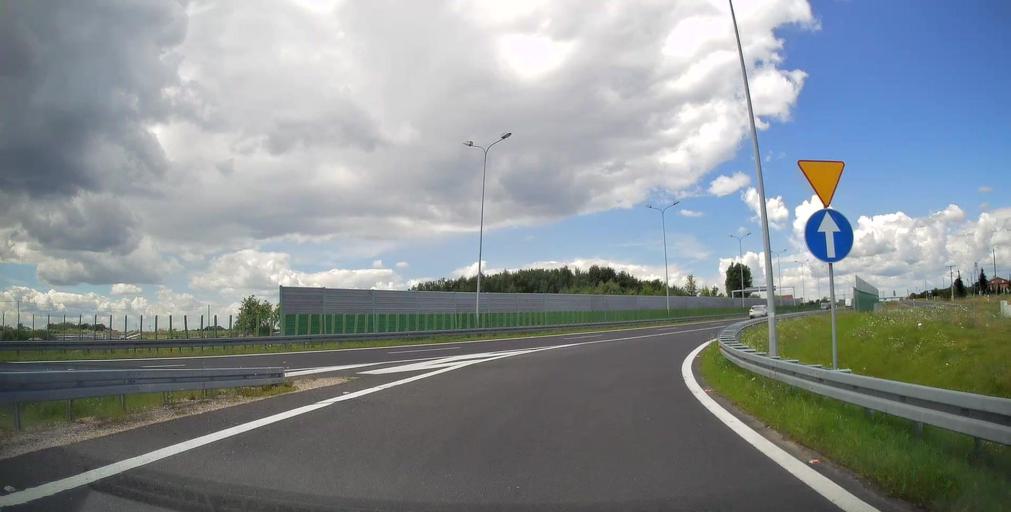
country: PL
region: Masovian Voivodeship
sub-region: Powiat grojecki
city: Goszczyn
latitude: 51.7600
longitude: 20.9065
